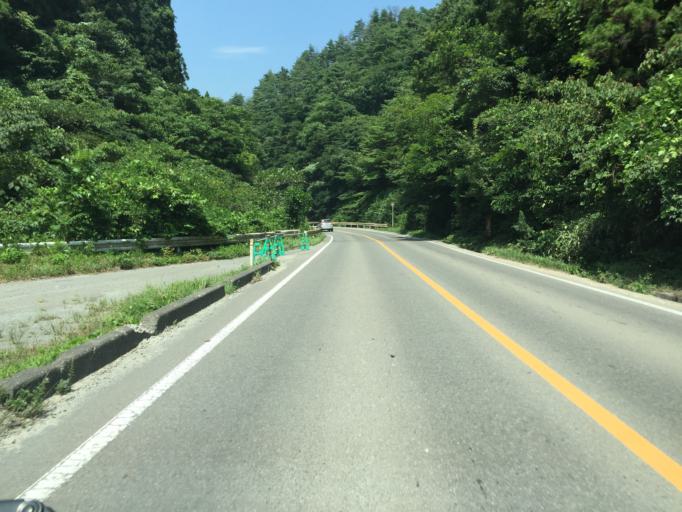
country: JP
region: Miyagi
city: Marumori
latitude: 37.8536
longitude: 140.8522
